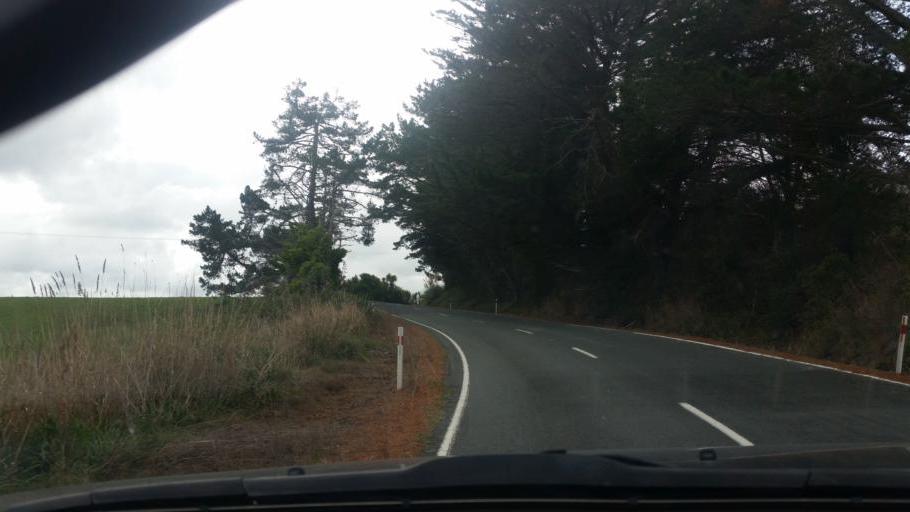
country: NZ
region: Auckland
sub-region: Auckland
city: Wellsford
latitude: -36.1440
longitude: 174.2847
